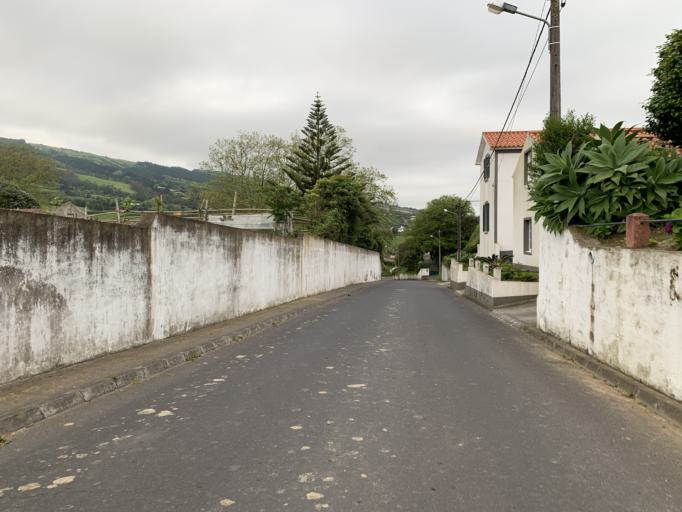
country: PT
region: Azores
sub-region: Ponta Delgada
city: Arrifes
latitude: 37.8485
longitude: -25.8419
